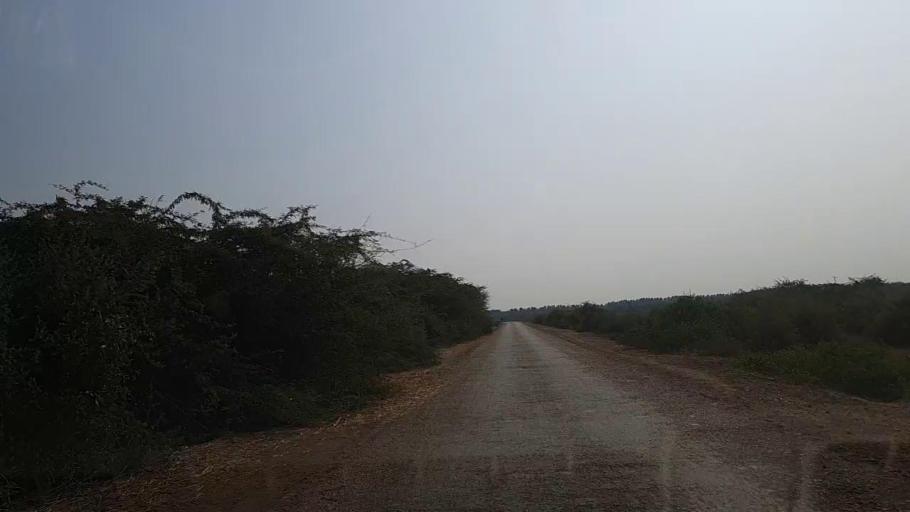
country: PK
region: Sindh
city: Keti Bandar
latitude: 24.2281
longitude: 67.6649
